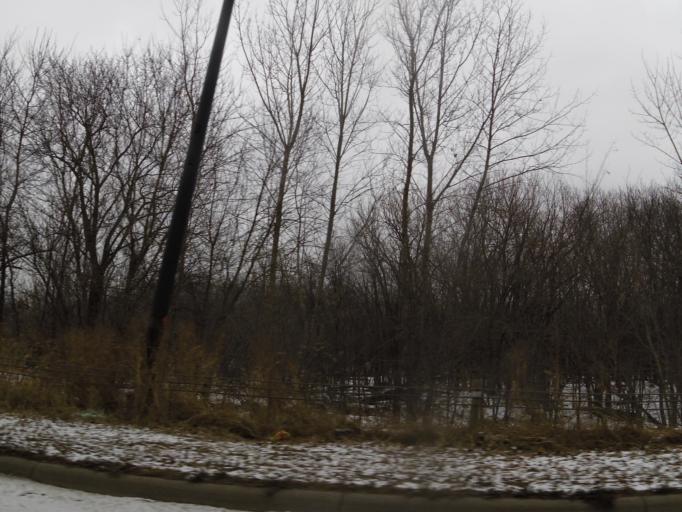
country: US
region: Minnesota
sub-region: Wright County
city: Delano
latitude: 45.0458
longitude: -93.7961
